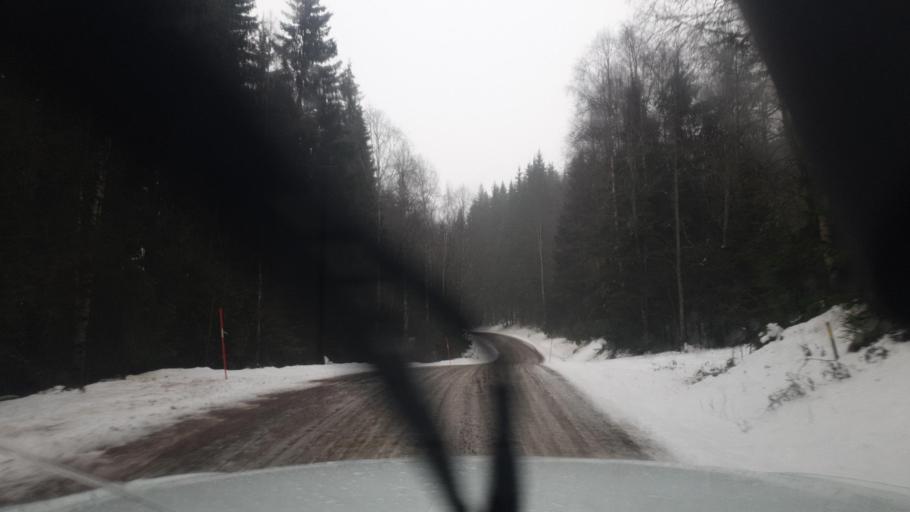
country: SE
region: Vaermland
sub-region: Eda Kommun
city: Charlottenberg
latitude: 60.0640
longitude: 12.5429
